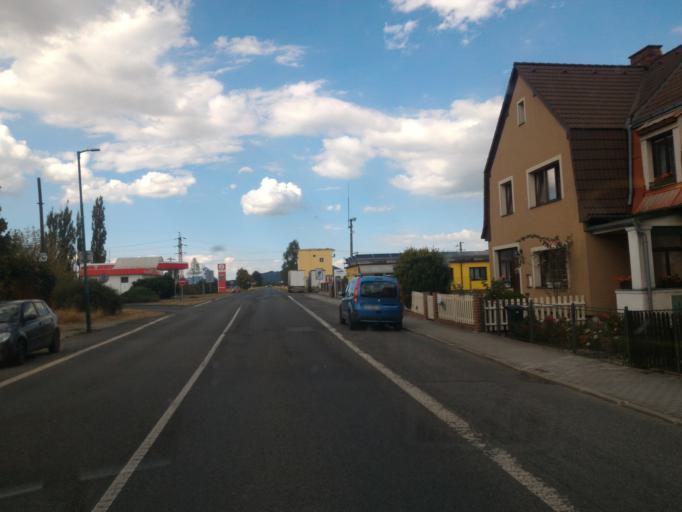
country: CZ
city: Mimon
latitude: 50.6672
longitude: 14.7269
